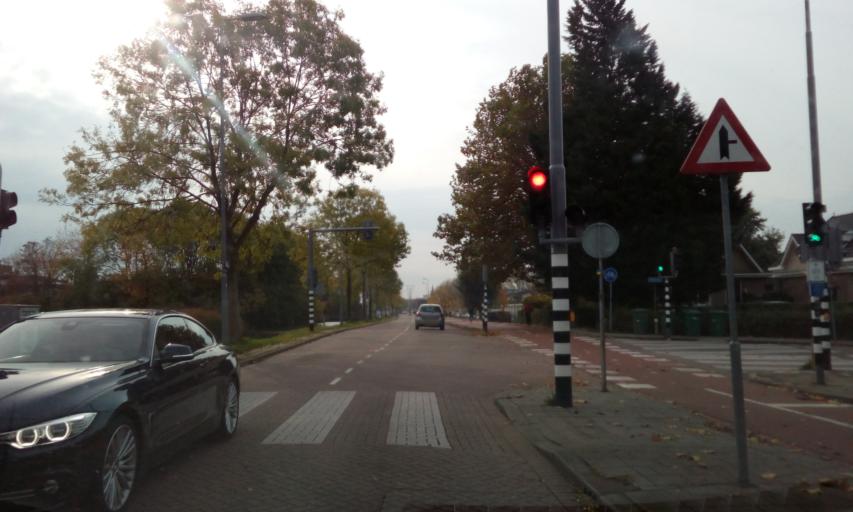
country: NL
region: South Holland
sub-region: Gemeente Rotterdam
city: Rotterdam
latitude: 51.9536
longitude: 4.4770
